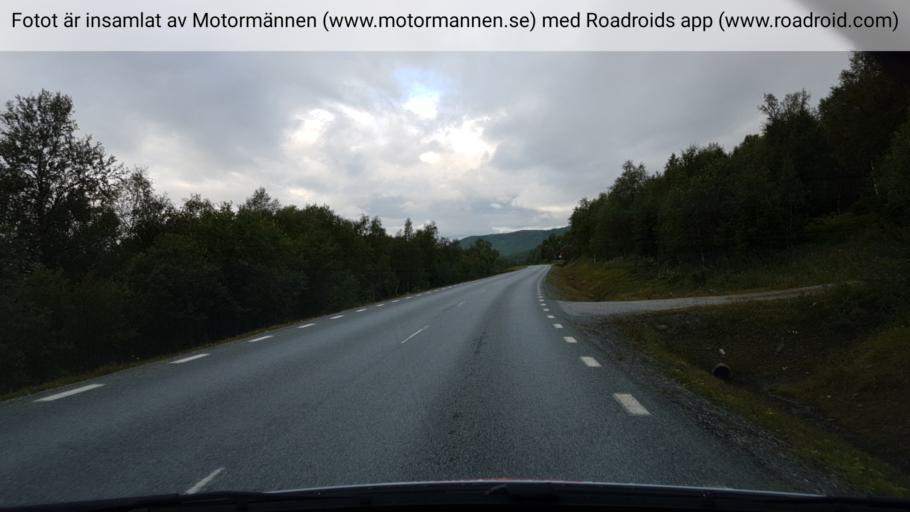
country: NO
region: Nordland
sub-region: Rana
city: Mo i Rana
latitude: 66.0421
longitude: 14.9926
